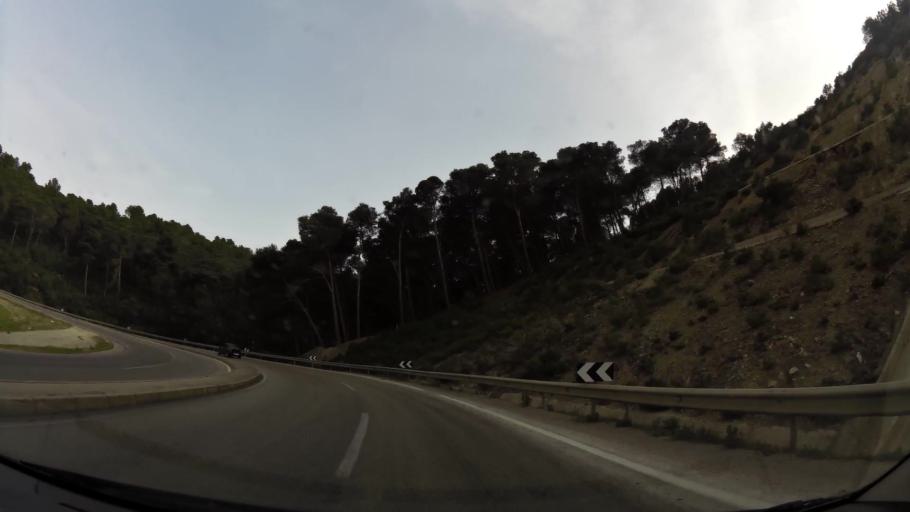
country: MA
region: Tanger-Tetouan
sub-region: Tanger-Assilah
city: Dar Chaoui
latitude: 35.5599
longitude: -5.5836
